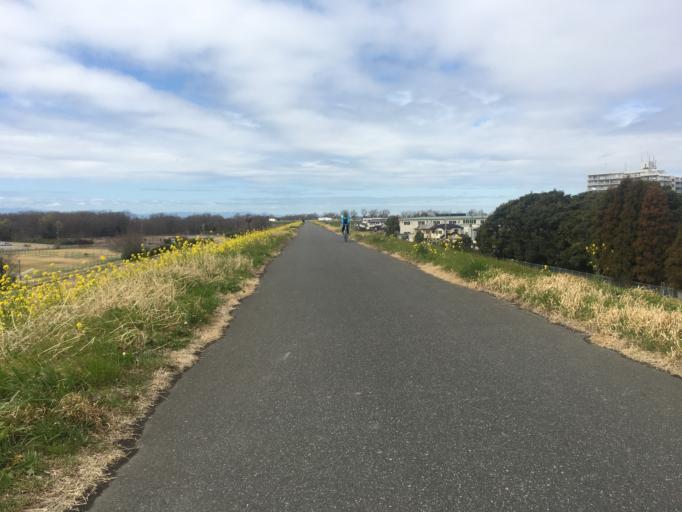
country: JP
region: Saitama
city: Shiki
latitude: 35.8570
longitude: 139.6021
